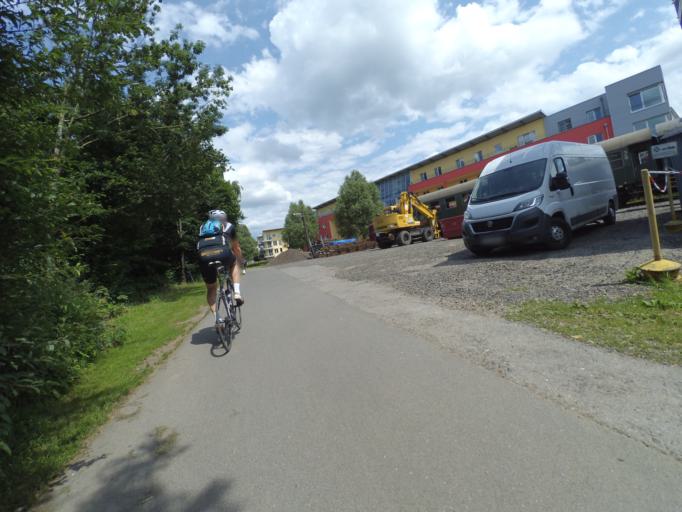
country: DE
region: North Rhine-Westphalia
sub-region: Regierungsbezirk Koln
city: Roetgen
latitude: 50.7033
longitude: 6.1773
